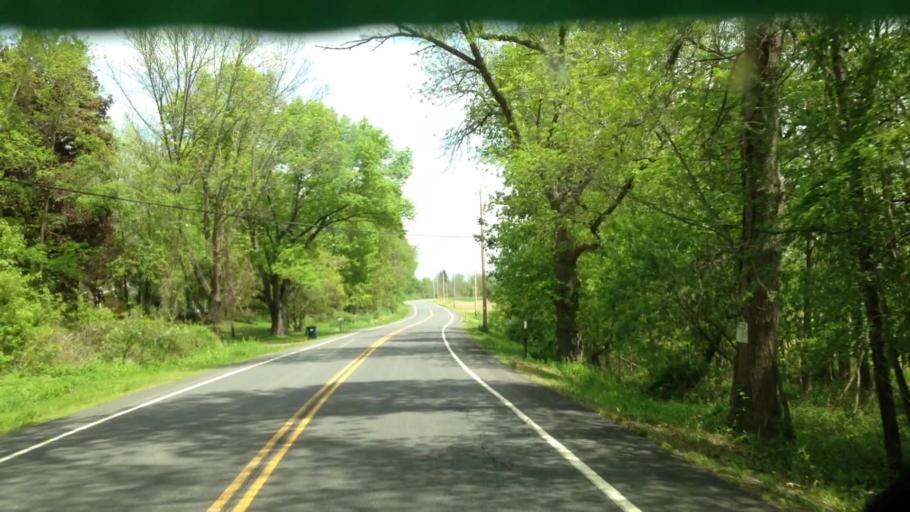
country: US
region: New York
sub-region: Dutchess County
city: Pine Plains
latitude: 42.0615
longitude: -73.6223
